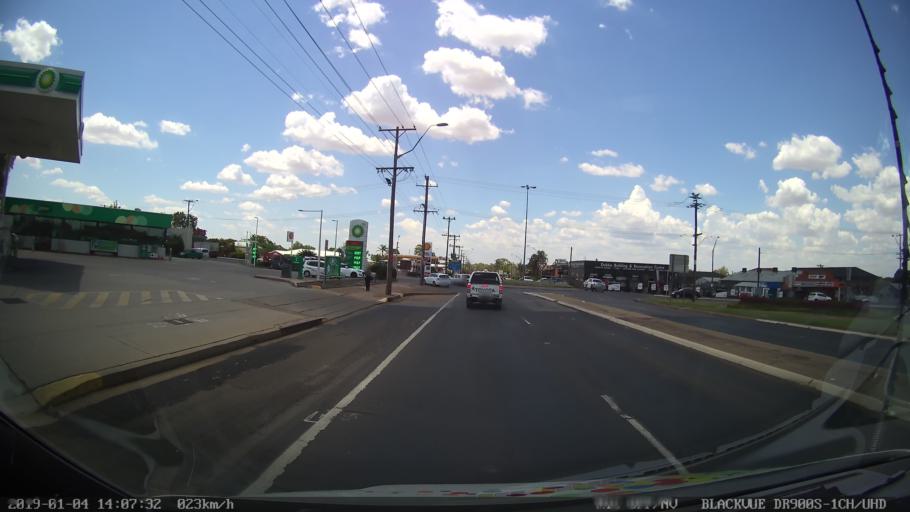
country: AU
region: New South Wales
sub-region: Dubbo Municipality
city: Dubbo
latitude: -32.2488
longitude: 148.5927
